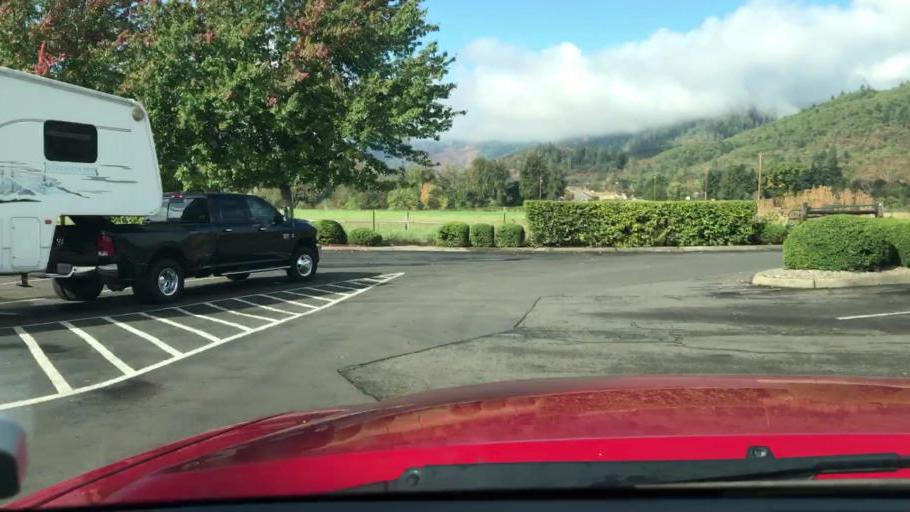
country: US
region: Oregon
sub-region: Douglas County
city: Tri-City
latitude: 42.9732
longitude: -123.3411
